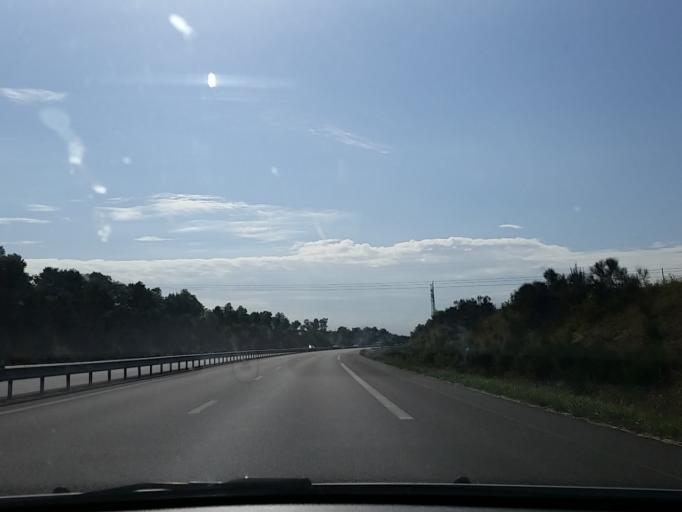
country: FR
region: Centre
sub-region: Departement du Cher
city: Trouy
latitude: 47.0353
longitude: 2.3680
